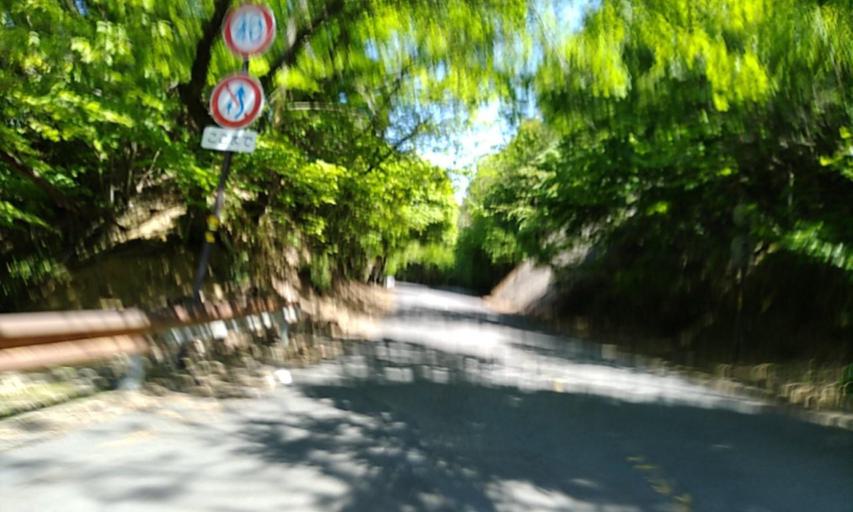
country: JP
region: Fukui
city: Obama
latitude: 35.5468
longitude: 135.7390
